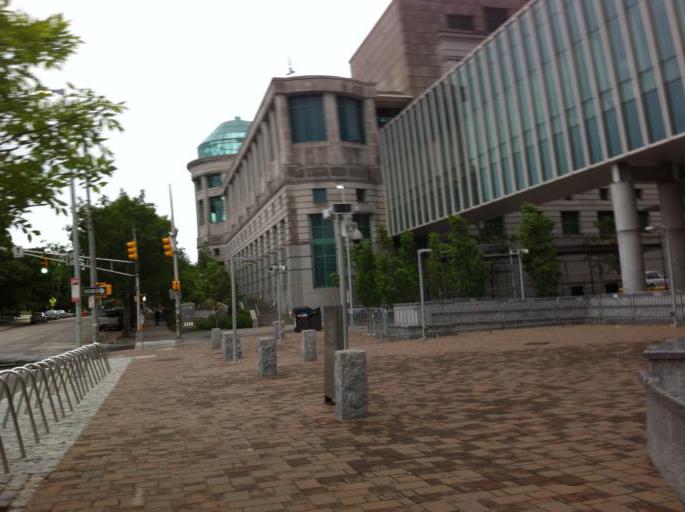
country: US
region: North Carolina
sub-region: Wake County
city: Raleigh
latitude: 35.7824
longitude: -78.6404
